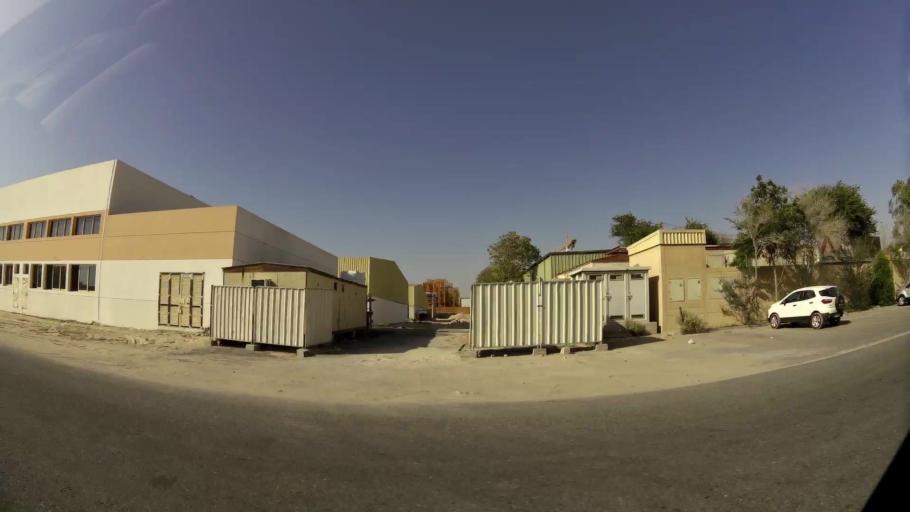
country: AE
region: Dubai
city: Dubai
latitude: 25.1224
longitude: 55.2141
